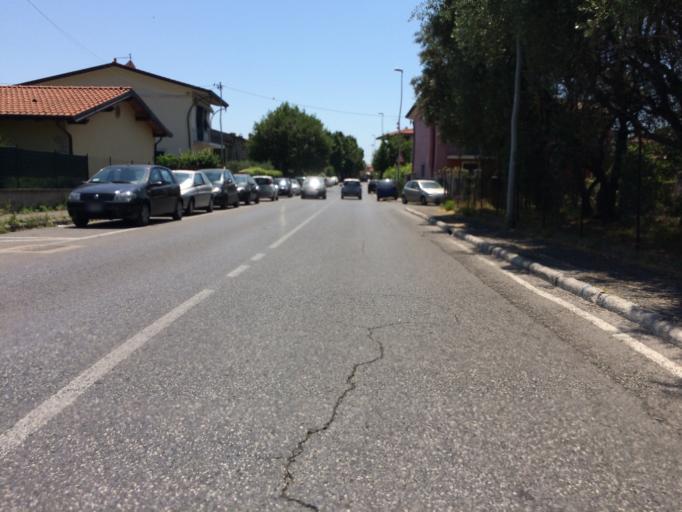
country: IT
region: Tuscany
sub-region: Provincia di Massa-Carrara
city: Massa
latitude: 44.0418
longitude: 10.1338
